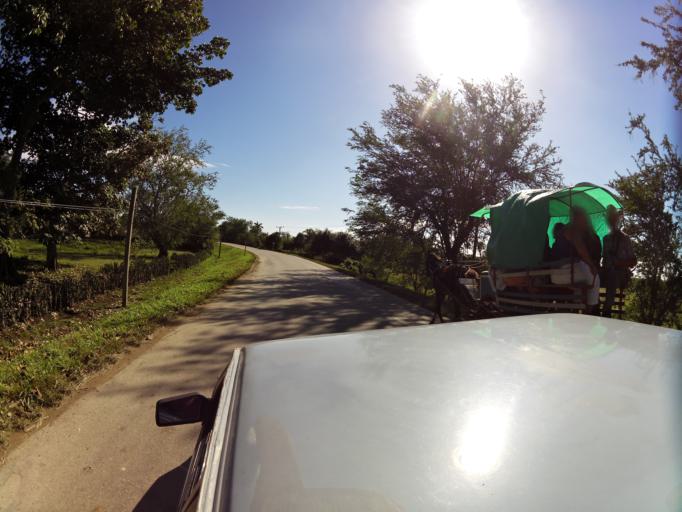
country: CU
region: Las Tunas
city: Las Tunas
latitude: 20.9809
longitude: -76.8840
